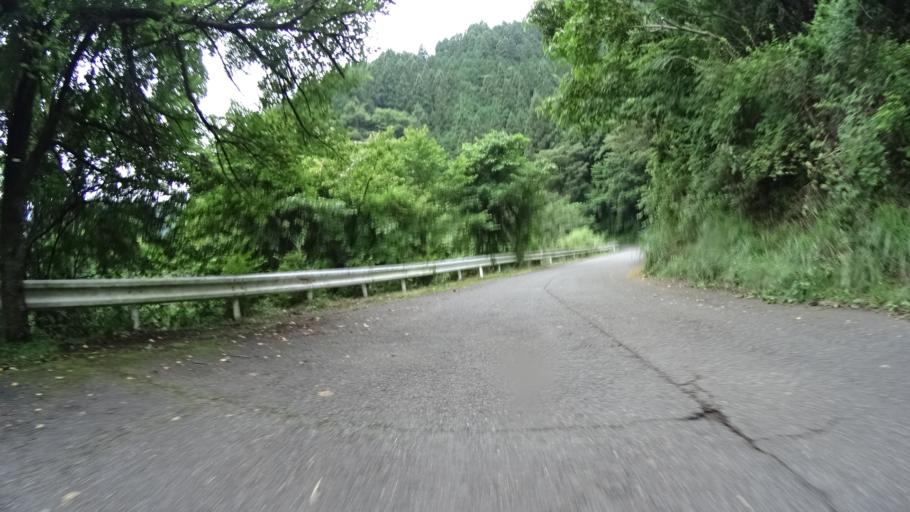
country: JP
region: Kanagawa
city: Hadano
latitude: 35.4791
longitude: 139.2109
